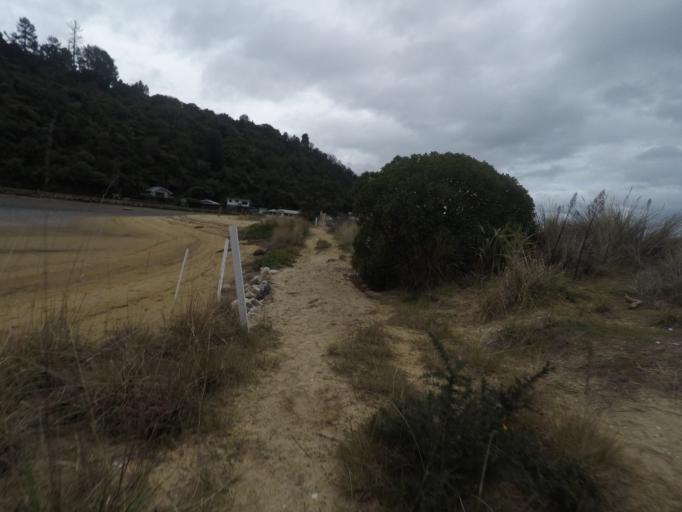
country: NZ
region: Tasman
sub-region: Tasman District
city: Motueka
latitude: -41.0102
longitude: 173.0073
